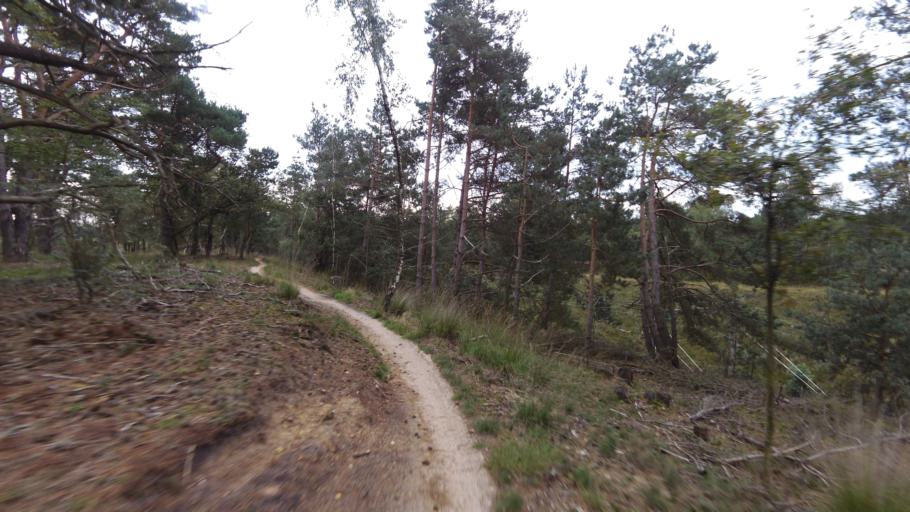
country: NL
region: Gelderland
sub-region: Gemeente Apeldoorn
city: Apeldoorn
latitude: 52.1973
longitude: 5.8685
